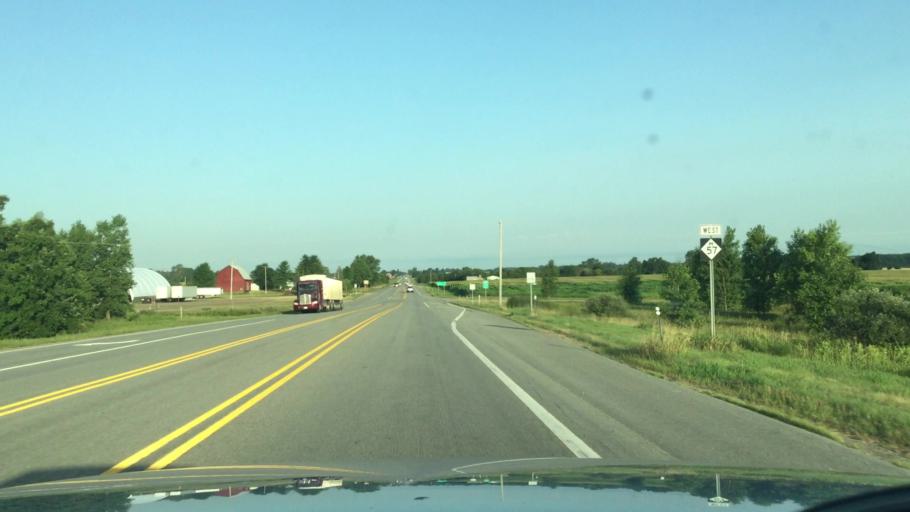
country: US
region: Michigan
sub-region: Gratiot County
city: Ithaca
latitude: 43.1761
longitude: -84.5670
